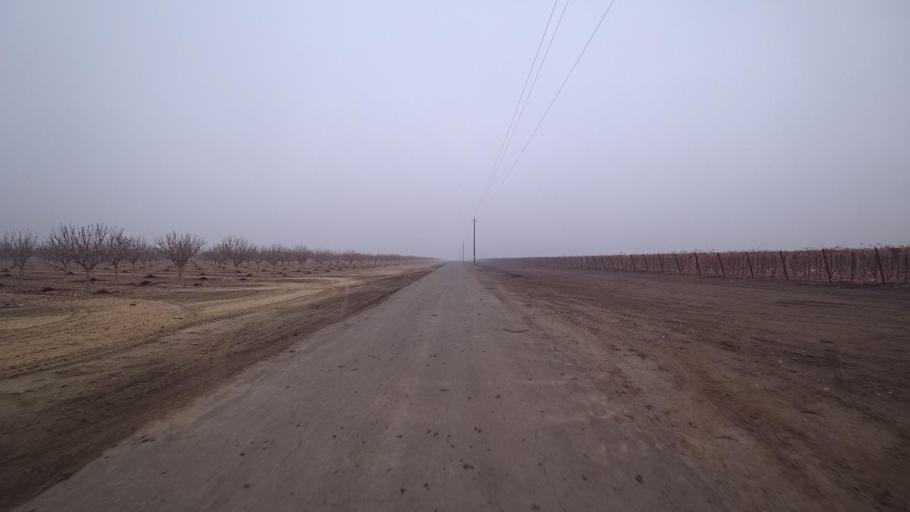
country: US
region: California
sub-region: Kern County
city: Buttonwillow
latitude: 35.4269
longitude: -119.5289
